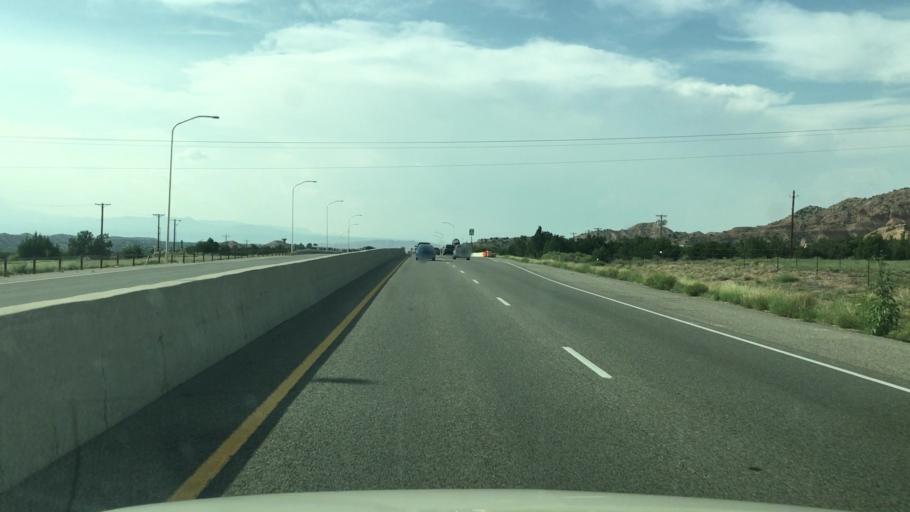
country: US
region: New Mexico
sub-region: Santa Fe County
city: Nambe
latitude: 35.8170
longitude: -105.9717
